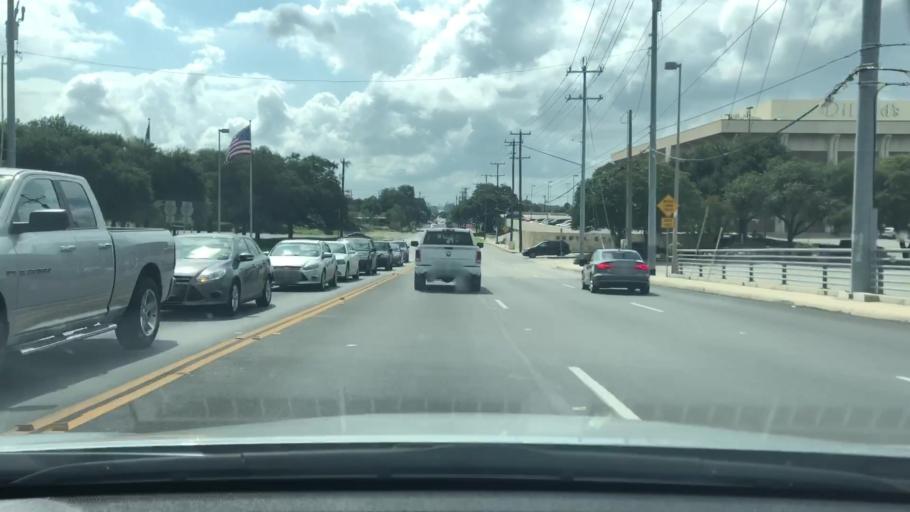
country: US
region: Texas
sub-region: Bexar County
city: Castle Hills
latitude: 29.5200
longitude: -98.4918
